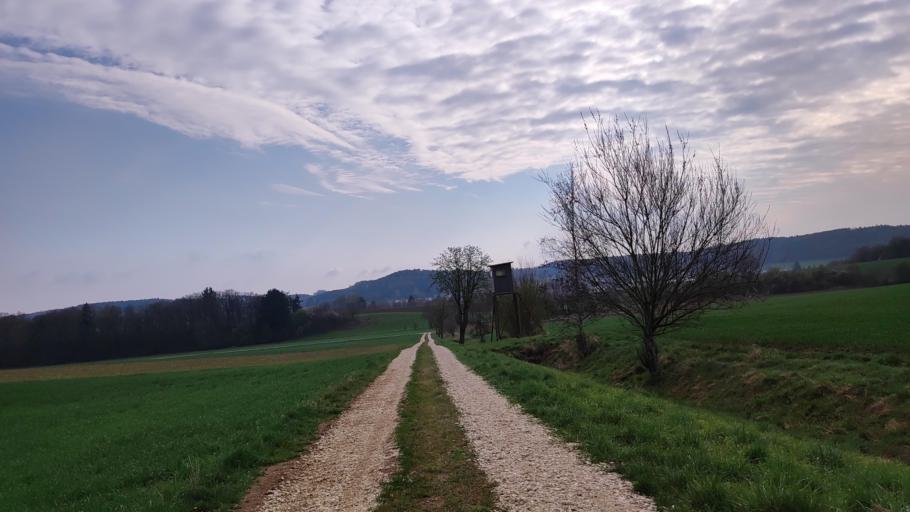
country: DE
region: Bavaria
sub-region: Swabia
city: Altenmunster
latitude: 48.4366
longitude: 10.5819
